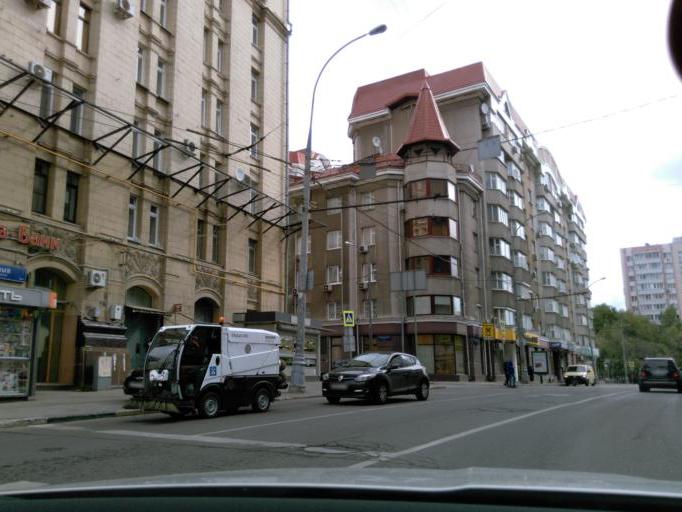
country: RU
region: Moscow
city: Mar'ina Roshcha
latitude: 55.7862
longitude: 37.6353
